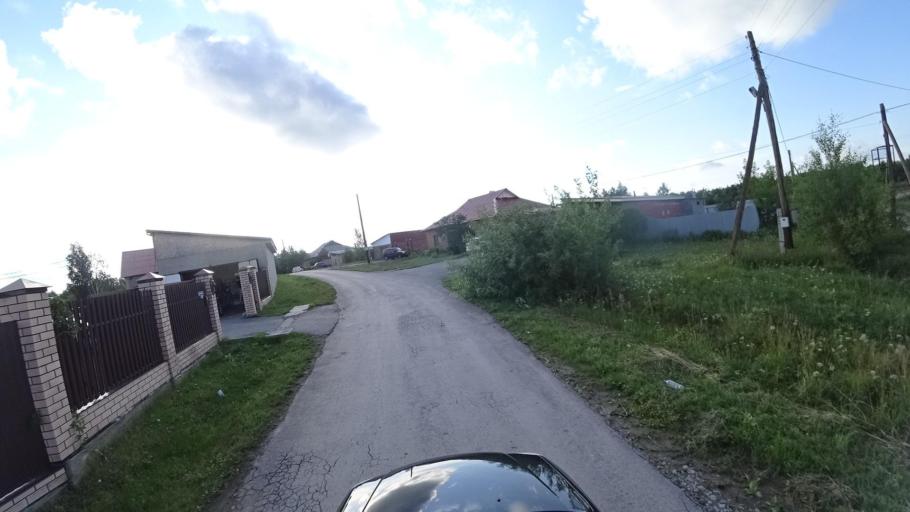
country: RU
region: Sverdlovsk
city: Obukhovskoye
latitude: 56.8508
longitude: 62.6520
